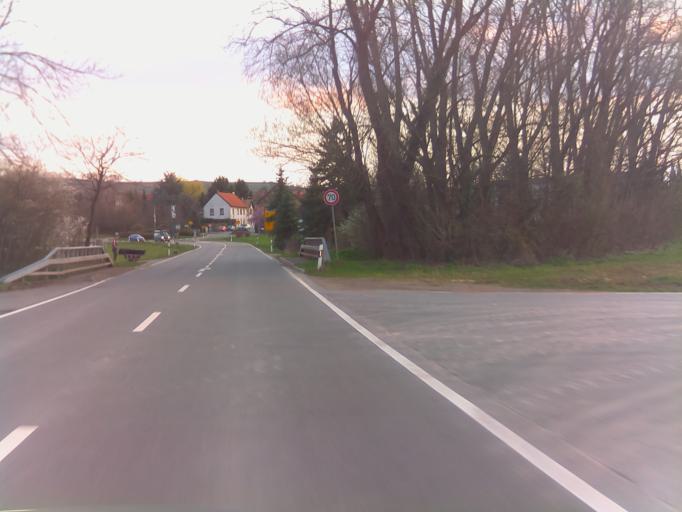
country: DE
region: Rheinland-Pfalz
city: Flonheim
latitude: 49.7912
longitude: 8.0454
